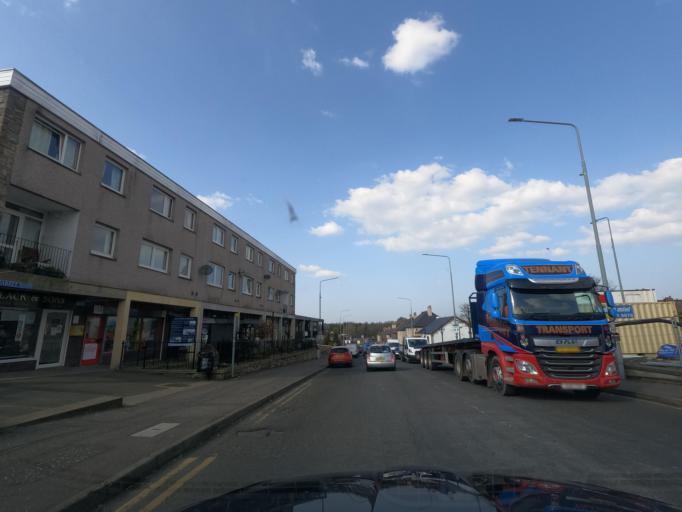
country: GB
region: Scotland
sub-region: West Lothian
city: Whitburn
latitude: 55.8669
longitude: -3.6852
